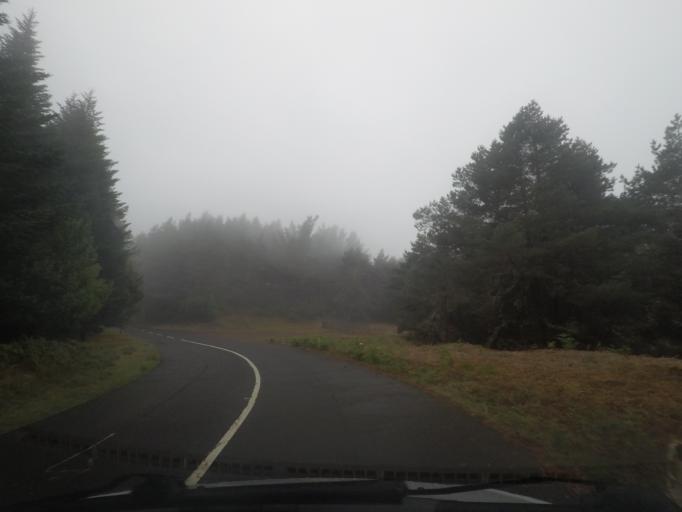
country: PT
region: Madeira
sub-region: Funchal
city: Nossa Senhora do Monte
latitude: 32.7152
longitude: -16.8845
